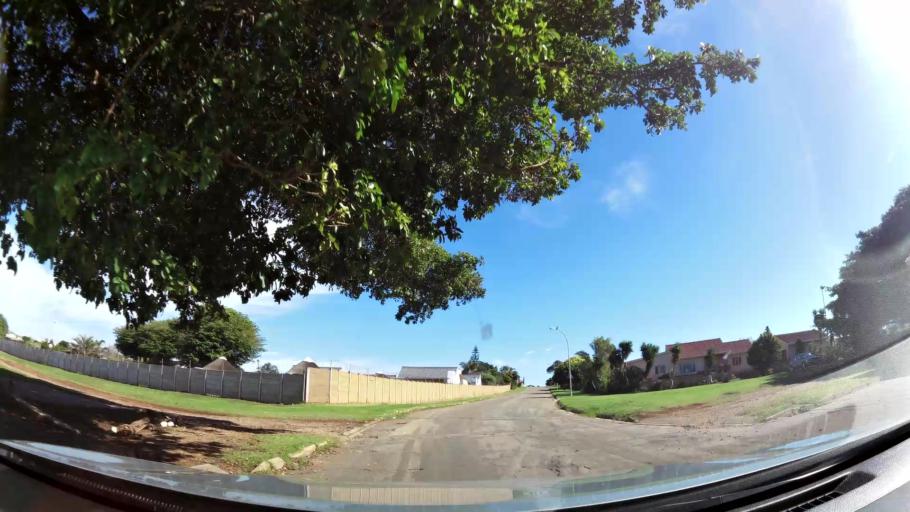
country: ZA
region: Eastern Cape
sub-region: Cacadu District Municipality
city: Jeffrey's Bay
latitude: -34.0522
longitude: 24.9188
